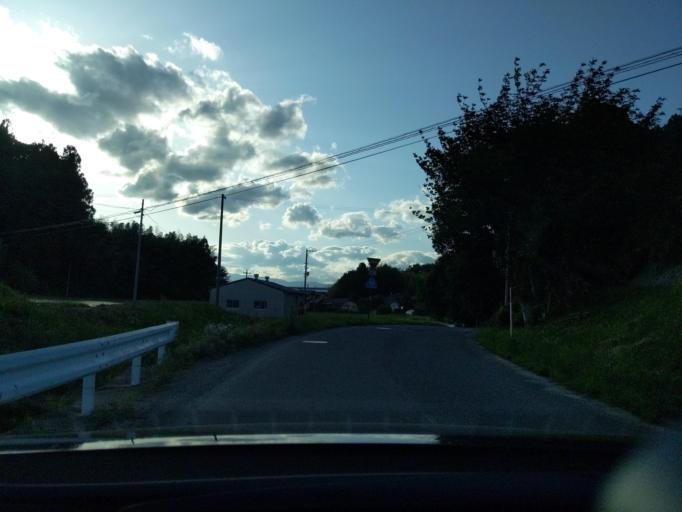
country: JP
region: Fukushima
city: Miharu
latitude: 37.4318
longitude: 140.4341
